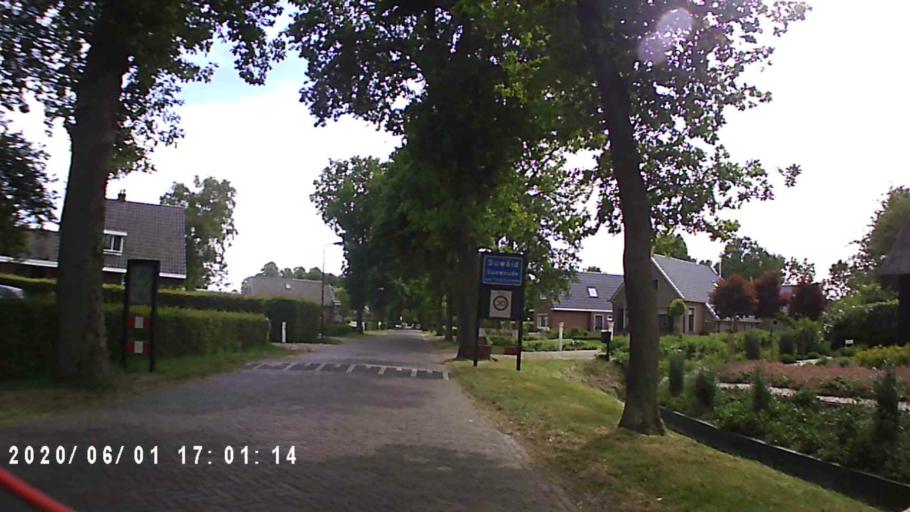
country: NL
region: Friesland
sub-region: Gemeente Tytsjerksteradiel
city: Hurdegaryp
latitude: 53.1810
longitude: 5.9285
